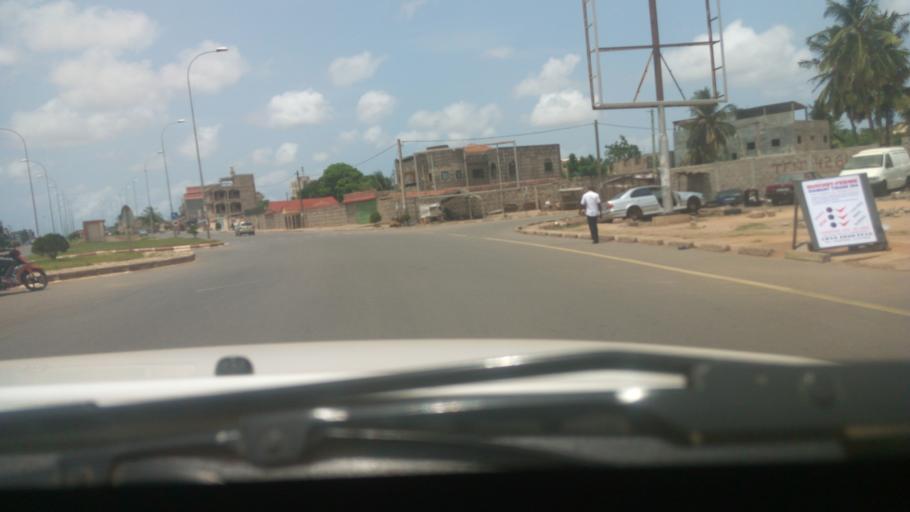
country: TG
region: Maritime
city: Lome
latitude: 6.2037
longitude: 1.1907
